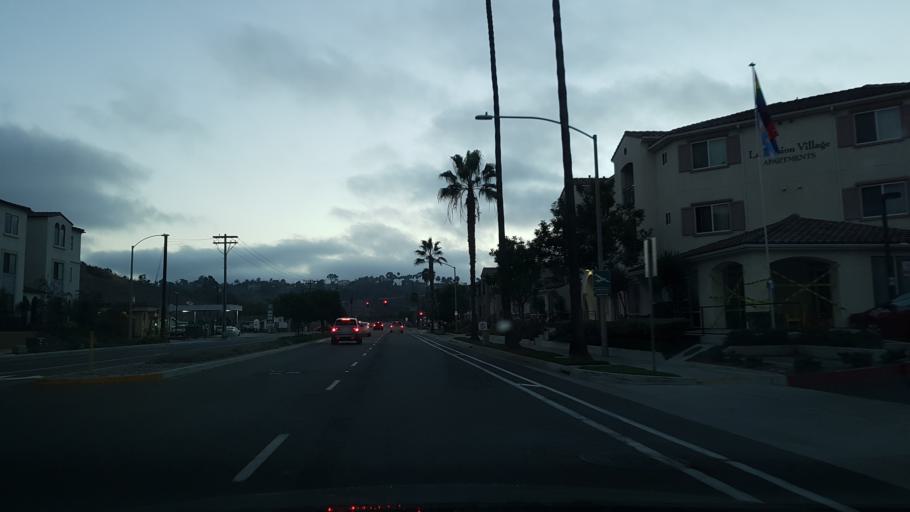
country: US
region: California
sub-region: San Diego County
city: Camp Pendleton South
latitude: 33.2144
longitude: -117.3470
